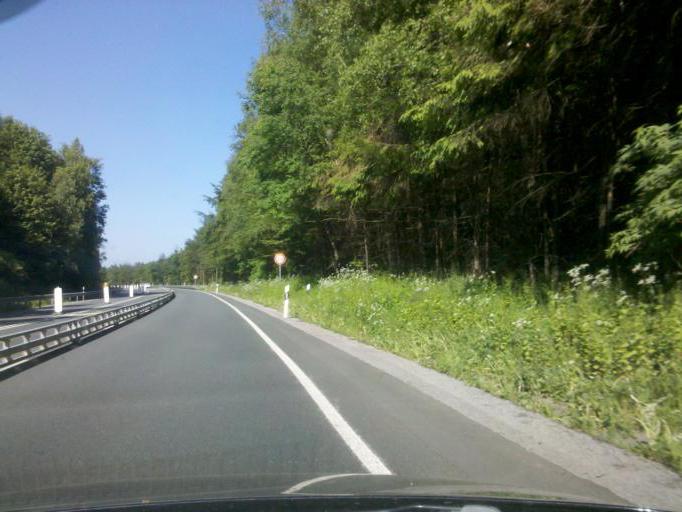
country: DE
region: North Rhine-Westphalia
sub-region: Regierungsbezirk Arnsberg
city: Burbach
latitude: 50.7475
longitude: 8.1401
